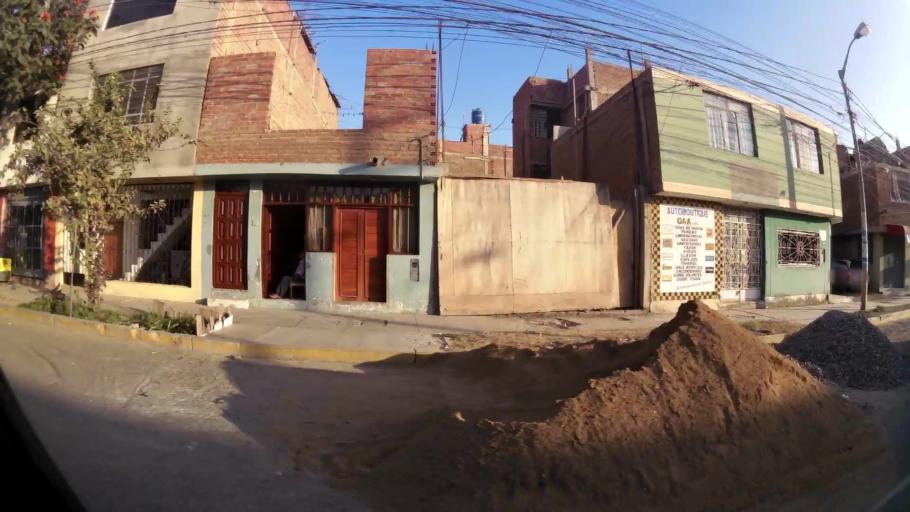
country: PE
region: Lambayeque
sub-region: Provincia de Chiclayo
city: Santa Rosa
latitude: -6.7750
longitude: -79.8331
